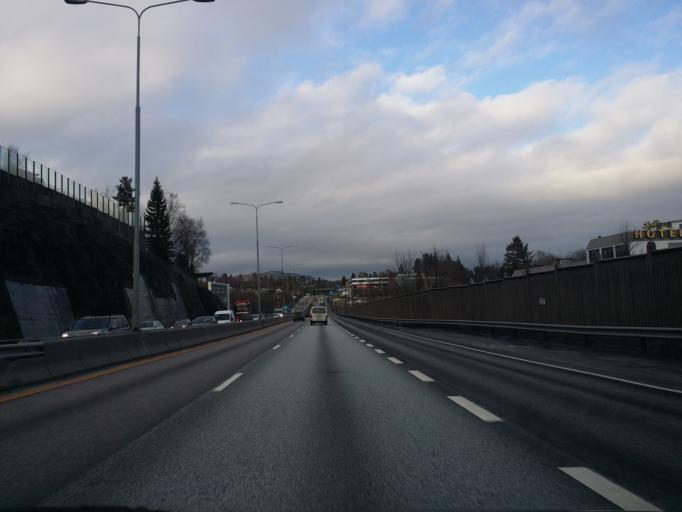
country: NO
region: Akershus
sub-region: Asker
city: Billingstad
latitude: 59.8640
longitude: 10.4871
